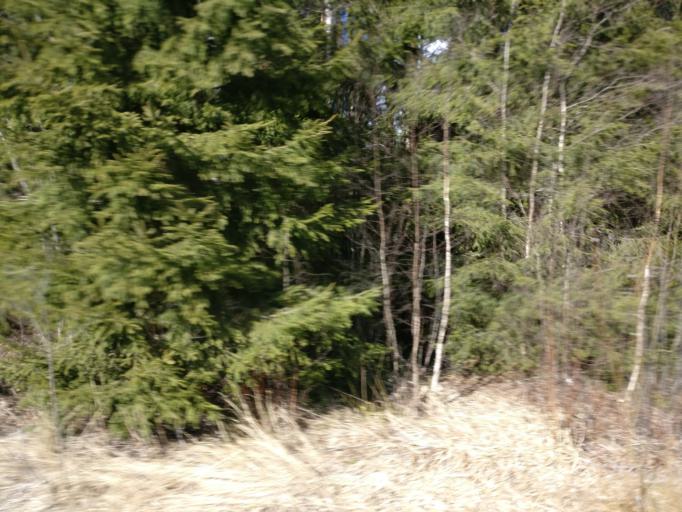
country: FI
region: Varsinais-Suomi
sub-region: Salo
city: Suomusjaervi
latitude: 60.3500
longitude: 23.6686
